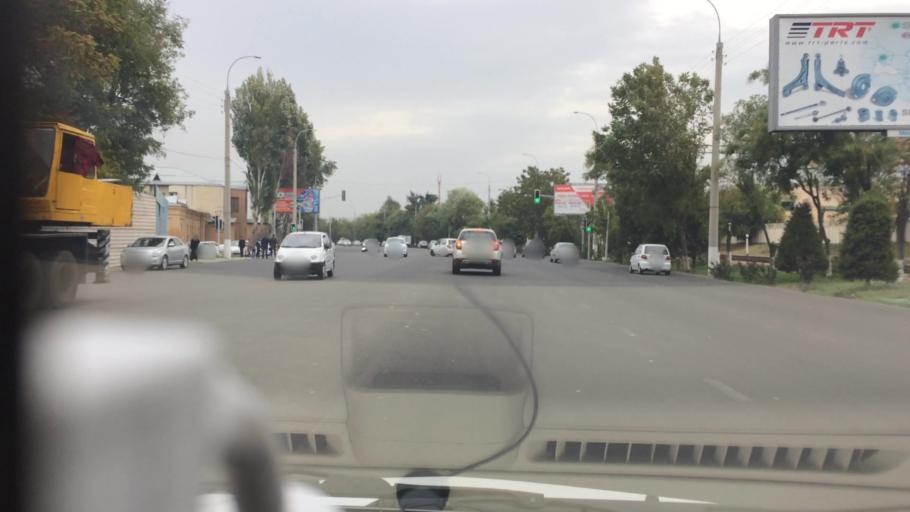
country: UZ
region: Toshkent Shahri
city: Tashkent
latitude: 41.3090
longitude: 69.3043
